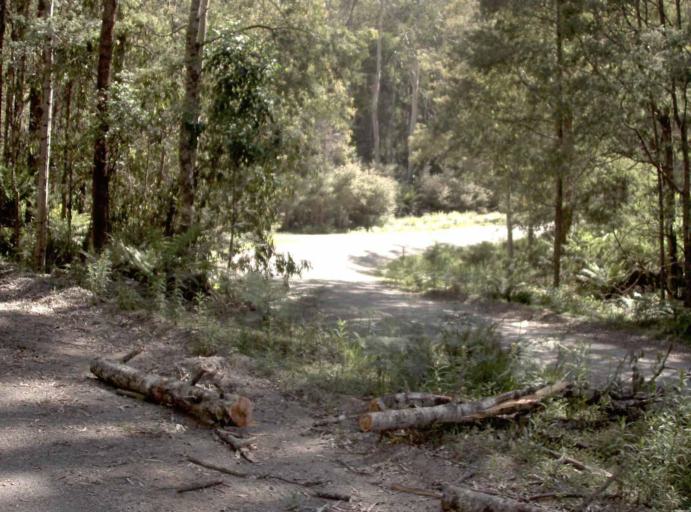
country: AU
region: New South Wales
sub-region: Bombala
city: Bombala
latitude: -37.2429
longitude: 148.7575
